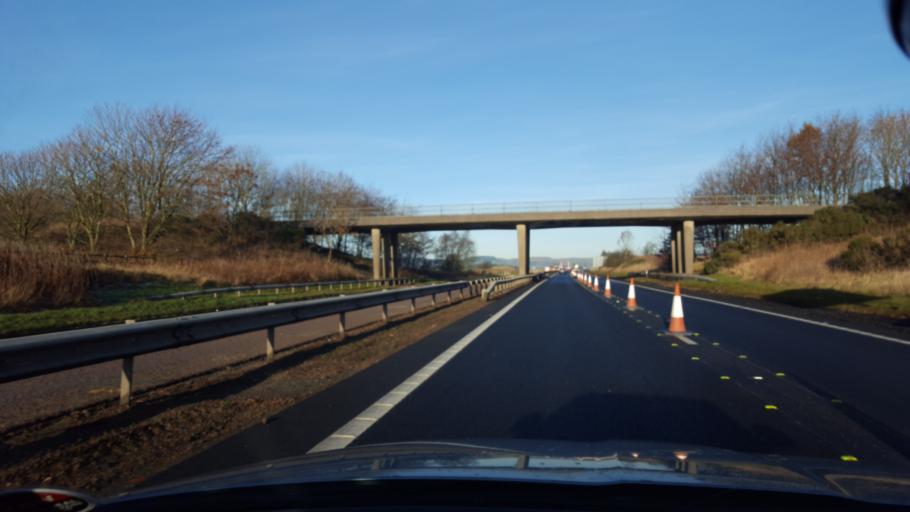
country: GB
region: Scotland
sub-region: Perth and Kinross
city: Kinross
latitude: 56.1763
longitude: -3.4110
